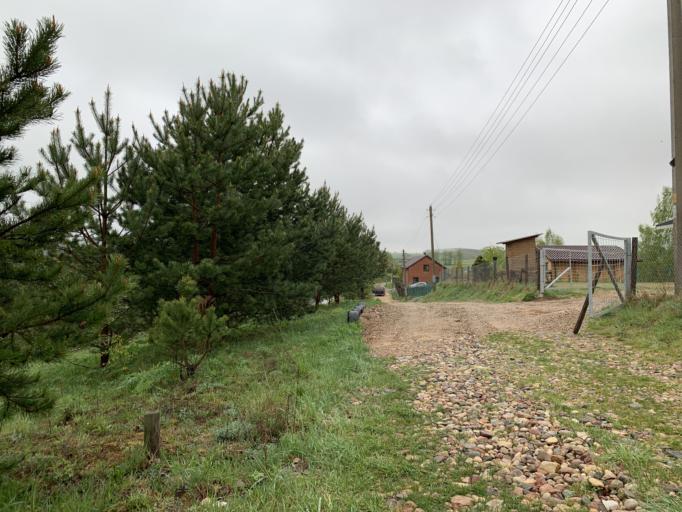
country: BY
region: Minsk
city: Lahoysk
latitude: 54.1229
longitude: 27.9026
